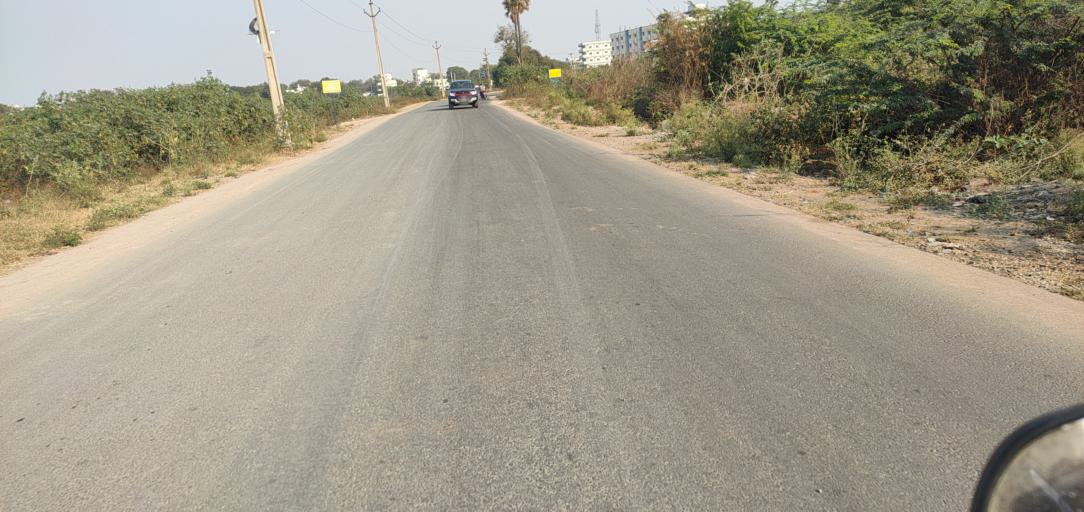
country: IN
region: Telangana
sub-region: Rangareddi
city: Lal Bahadur Nagar
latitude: 17.3423
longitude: 78.6206
